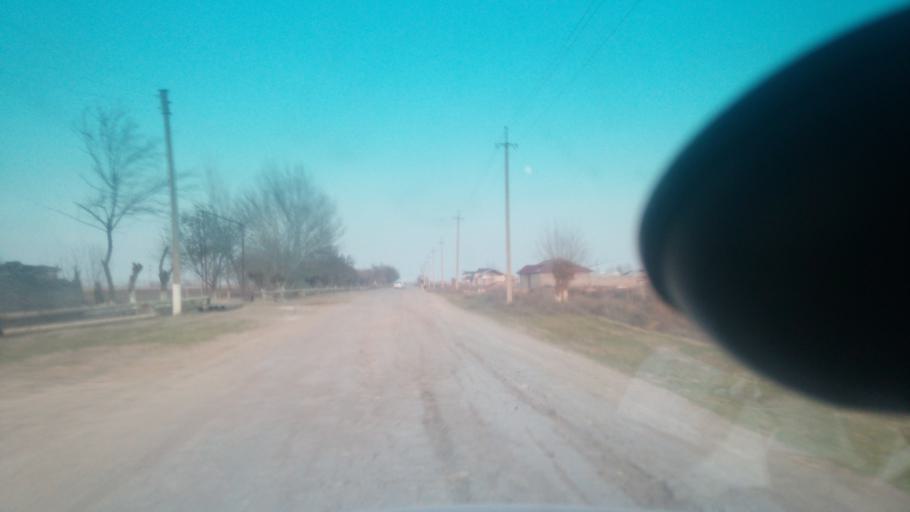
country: UZ
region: Sirdaryo
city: Guliston
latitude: 40.5258
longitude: 68.7826
